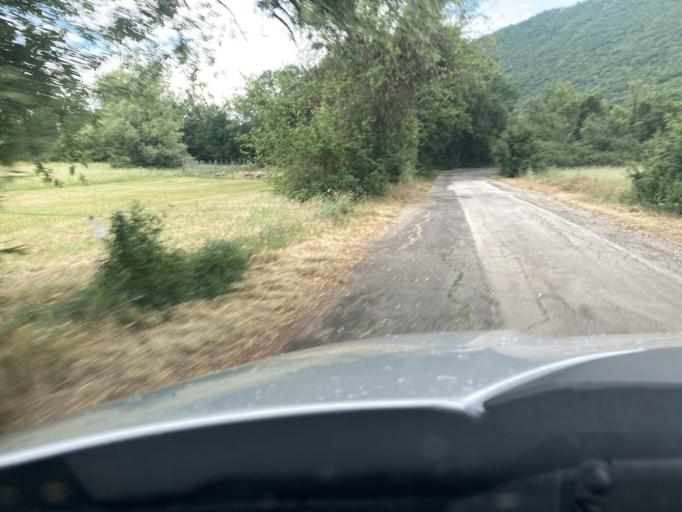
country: IT
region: Abruzzo
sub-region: Provincia dell' Aquila
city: San Panfilo d'Ocre
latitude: 42.2839
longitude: 13.4799
